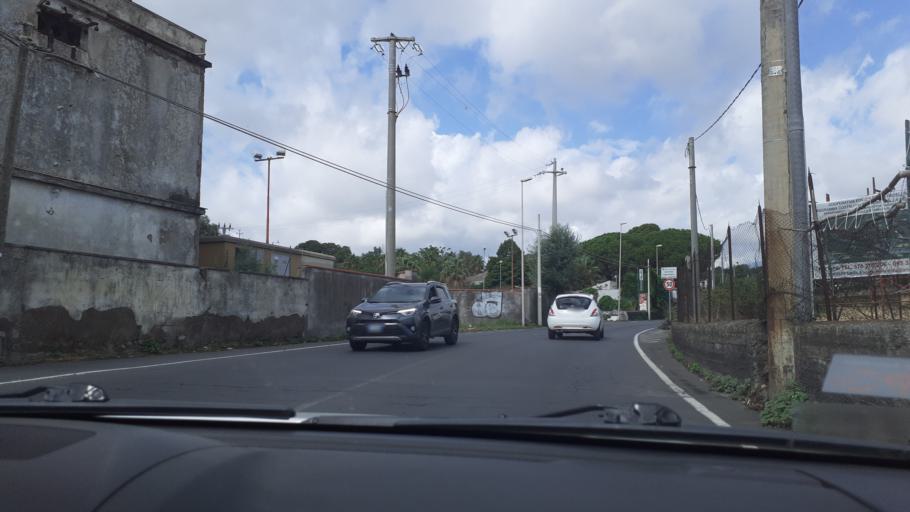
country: IT
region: Sicily
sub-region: Catania
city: San Giovanni la Punta
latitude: 37.5889
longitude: 15.0868
